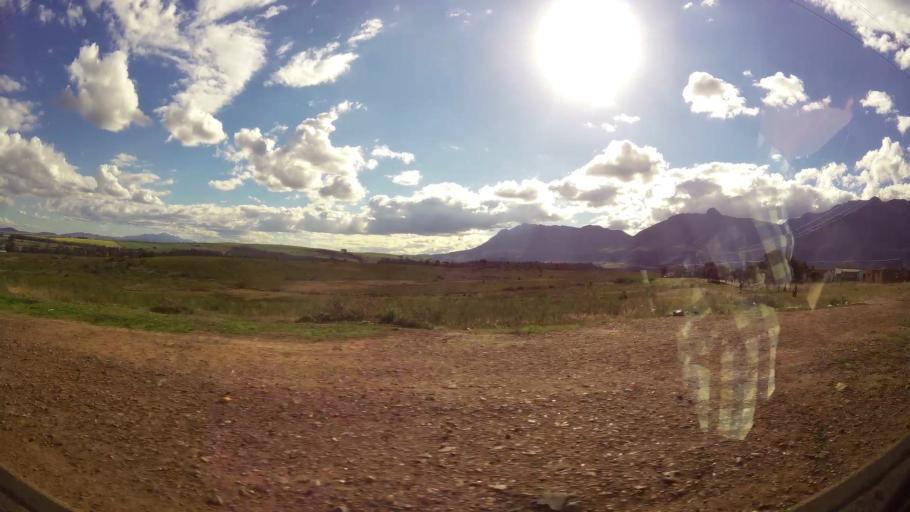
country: ZA
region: Western Cape
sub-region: Overberg District Municipality
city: Swellendam
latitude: -34.0420
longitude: 20.4408
